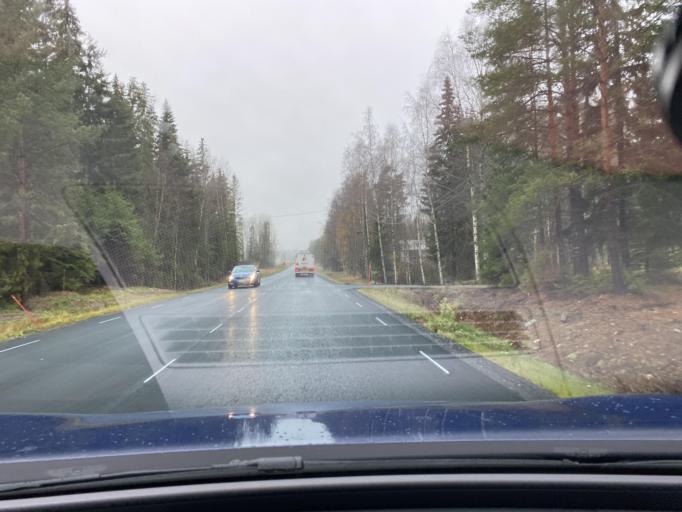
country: FI
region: Haeme
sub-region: Forssa
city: Ypaejae
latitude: 60.7752
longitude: 23.3366
